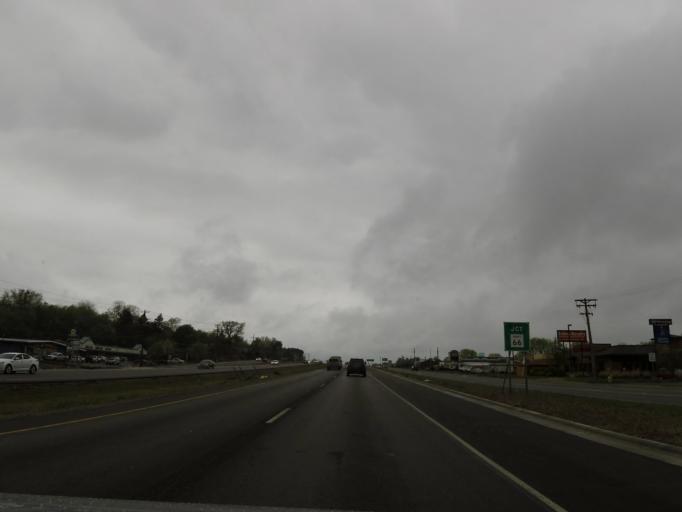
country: US
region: Minnesota
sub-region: Washington County
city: Oak Park Heights
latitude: 45.0360
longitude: -92.8131
